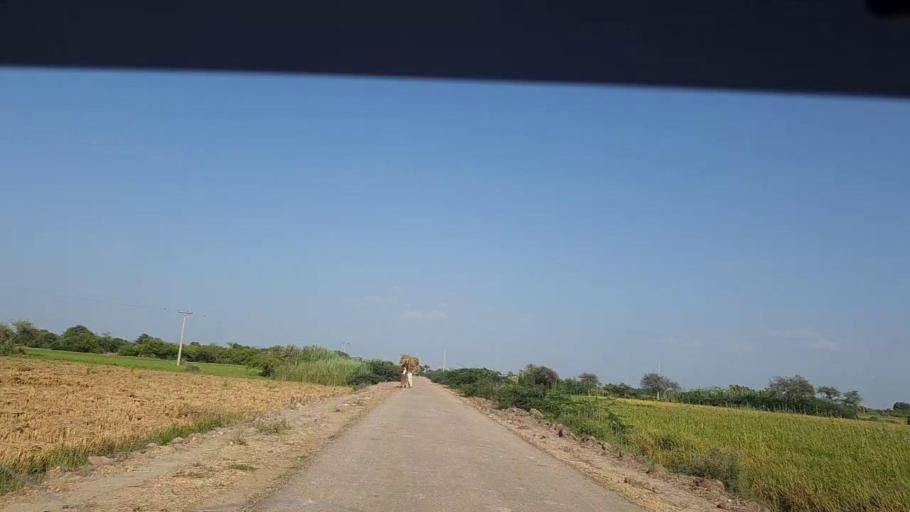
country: PK
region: Sindh
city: Kadhan
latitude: 24.4637
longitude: 68.8490
